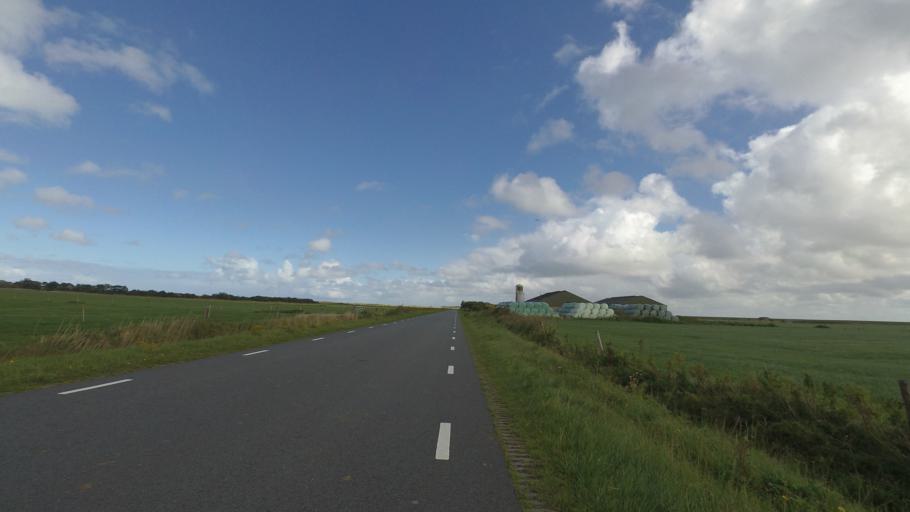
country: NL
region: Friesland
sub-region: Gemeente Ameland
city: Nes
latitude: 53.4491
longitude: 5.8120
